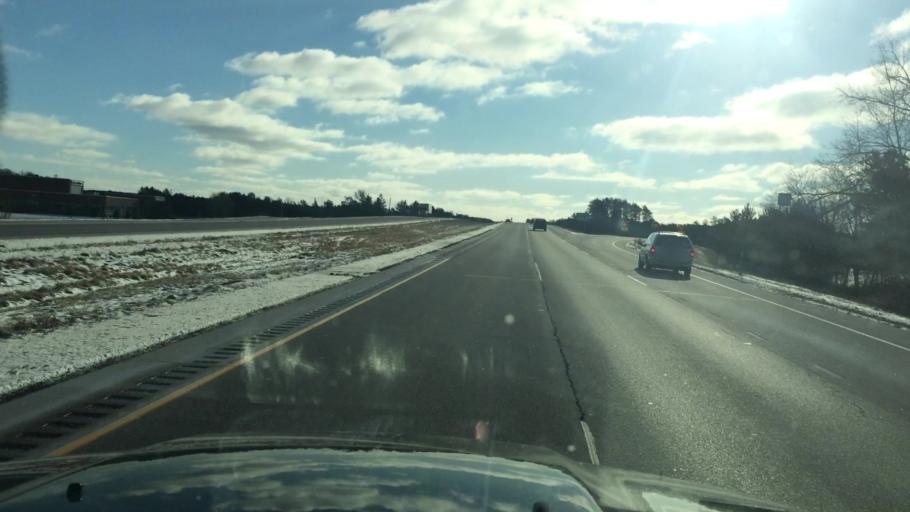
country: US
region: Wisconsin
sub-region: Portage County
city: Stevens Point
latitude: 44.5437
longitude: -89.5475
